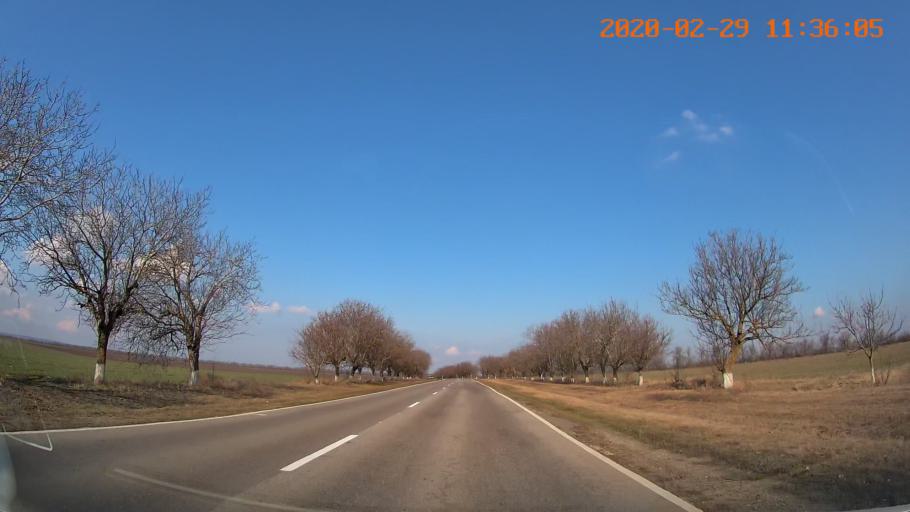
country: MD
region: Rezina
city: Saharna
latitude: 47.5906
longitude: 29.0589
